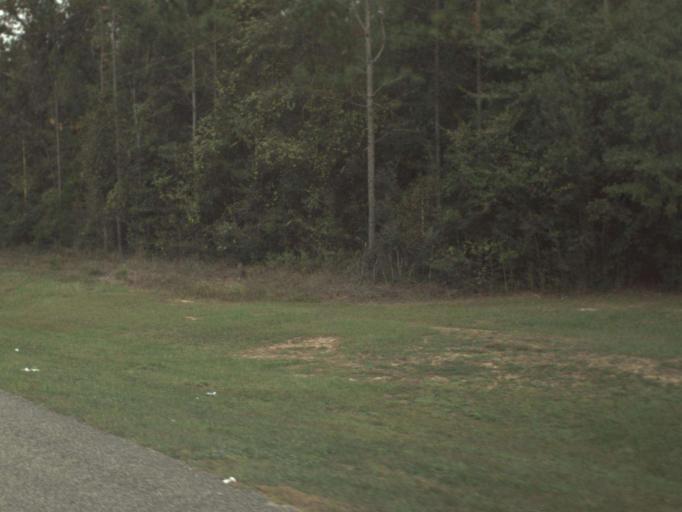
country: US
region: Florida
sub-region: Calhoun County
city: Blountstown
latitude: 30.5757
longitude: -85.1827
